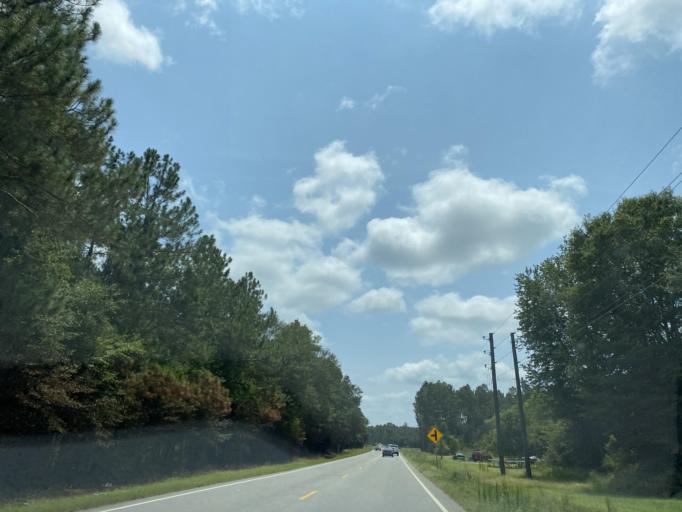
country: US
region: Georgia
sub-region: Jeff Davis County
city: Hazlehurst
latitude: 31.7989
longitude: -82.5656
